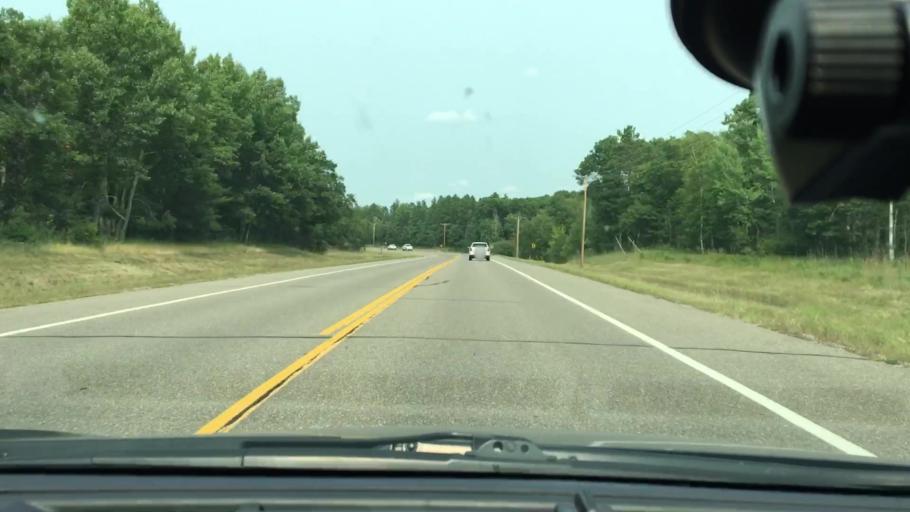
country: US
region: Minnesota
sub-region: Crow Wing County
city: Breezy Point
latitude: 46.5643
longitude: -94.1310
